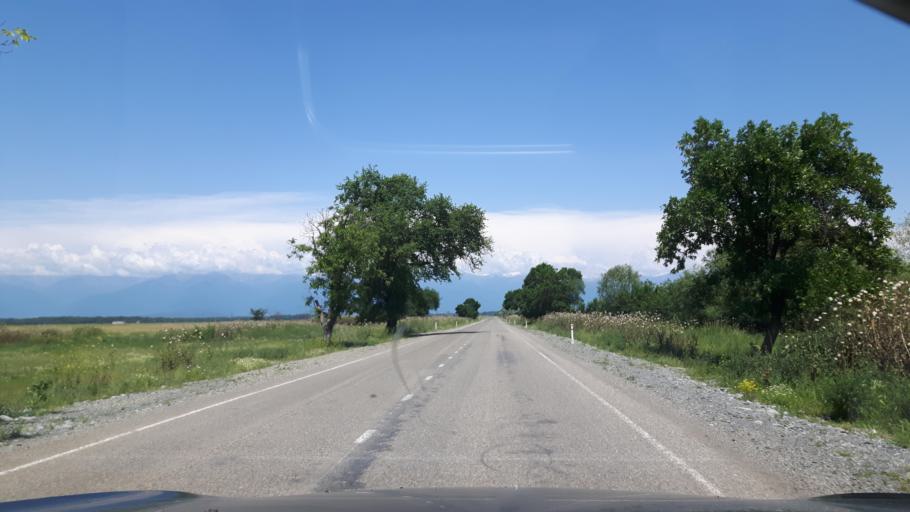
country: GE
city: Tsnori
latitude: 41.6382
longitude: 46.0339
